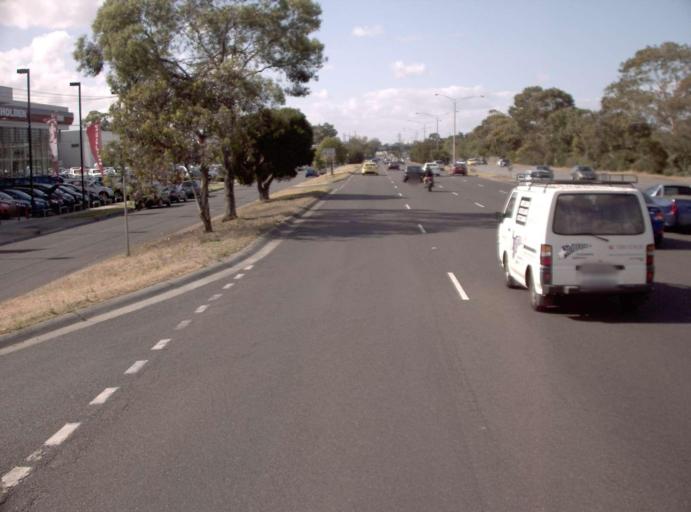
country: AU
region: Victoria
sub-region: Glen Eira
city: Elsternwick
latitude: -37.8905
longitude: 145.0021
